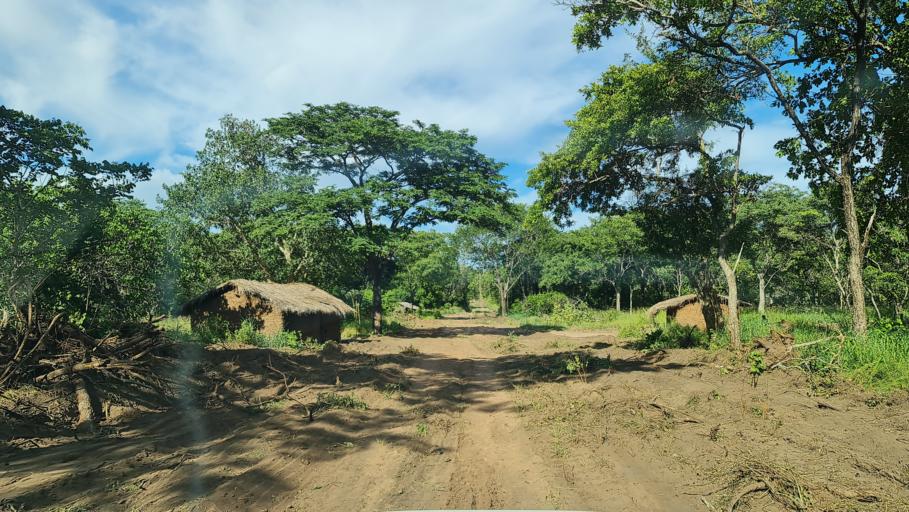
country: MZ
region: Nampula
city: Ilha de Mocambique
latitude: -15.5069
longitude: 40.1462
